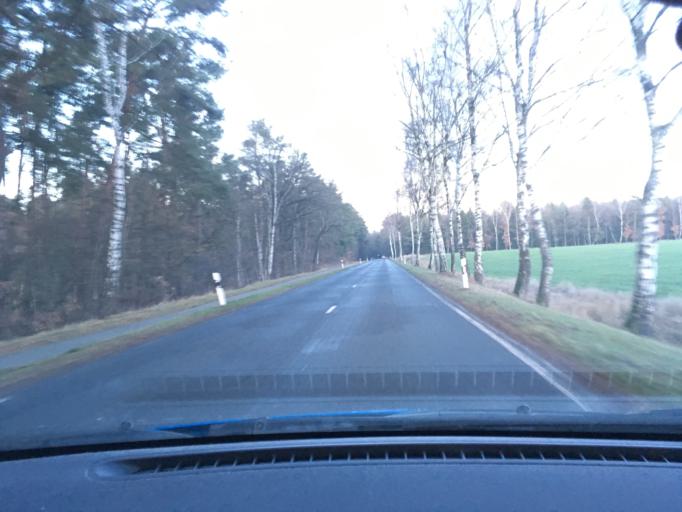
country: DE
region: Lower Saxony
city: Handeloh
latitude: 53.2453
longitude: 9.8714
